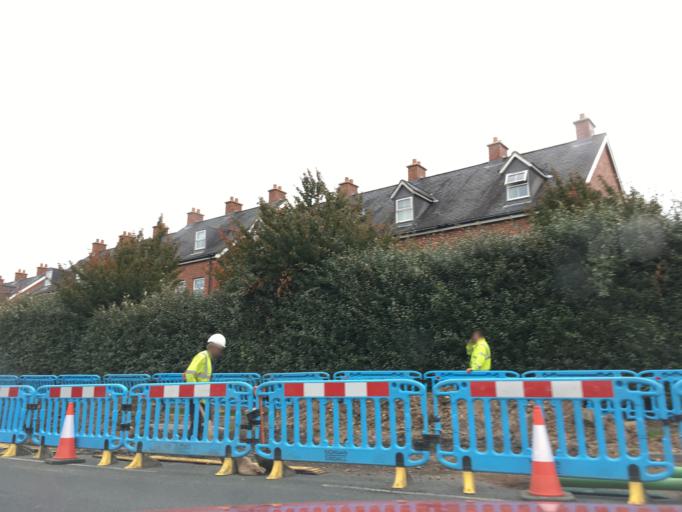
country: GB
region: England
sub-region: Gloucestershire
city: Stonehouse
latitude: 51.7519
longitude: -2.2830
